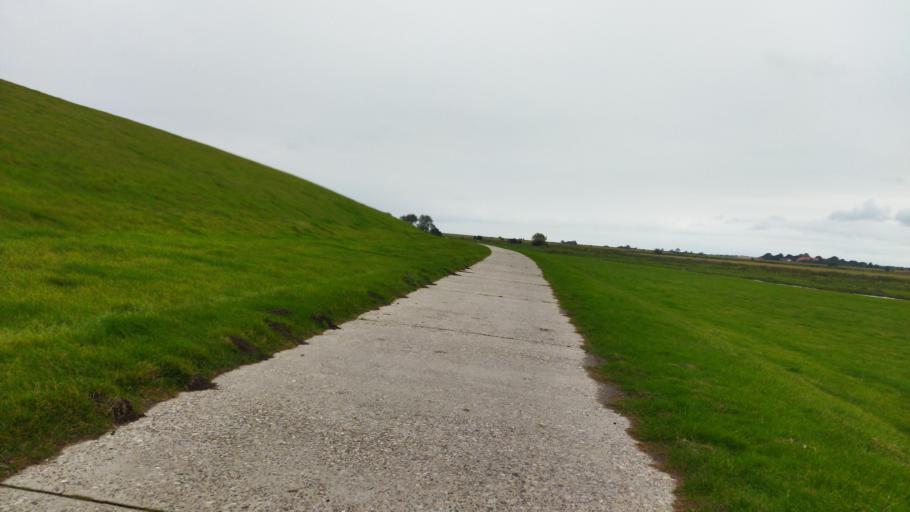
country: DE
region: Lower Saxony
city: Wirdum
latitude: 53.4932
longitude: 7.0411
